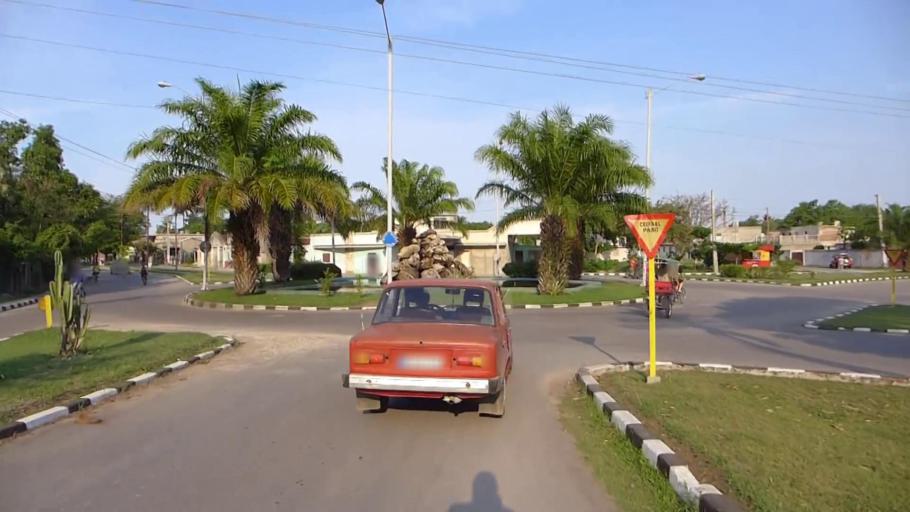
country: CU
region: Camaguey
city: Camaguey
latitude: 21.3833
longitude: -77.9072
